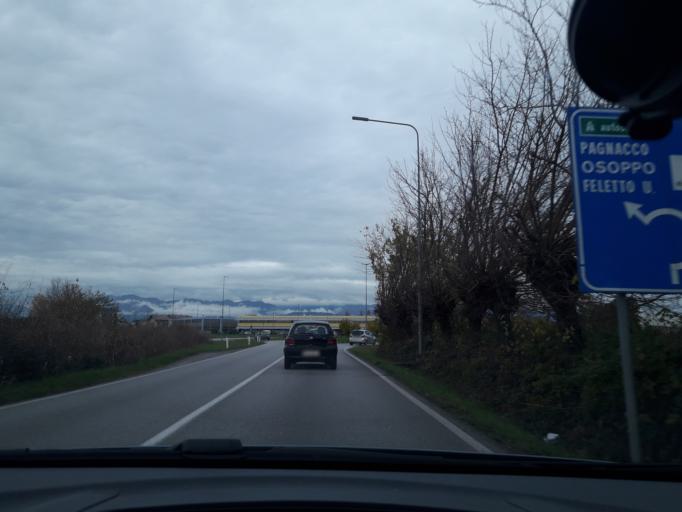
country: IT
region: Friuli Venezia Giulia
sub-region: Provincia di Udine
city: Colugna
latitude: 46.0920
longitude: 13.2145
